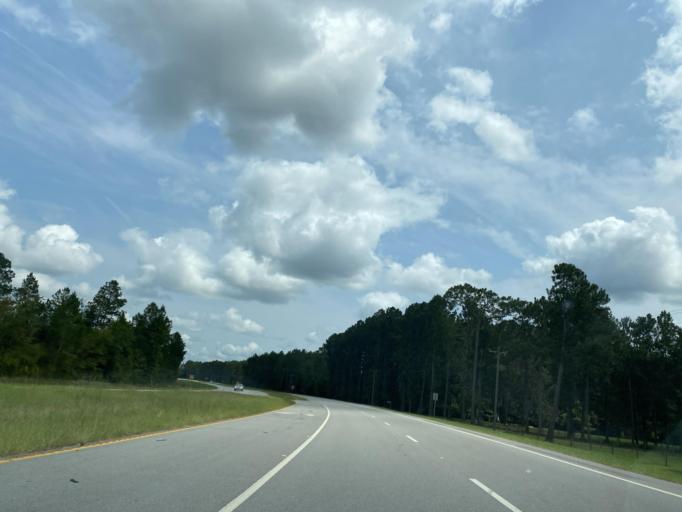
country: US
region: Georgia
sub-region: Ware County
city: Deenwood
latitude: 31.2766
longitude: -82.4499
